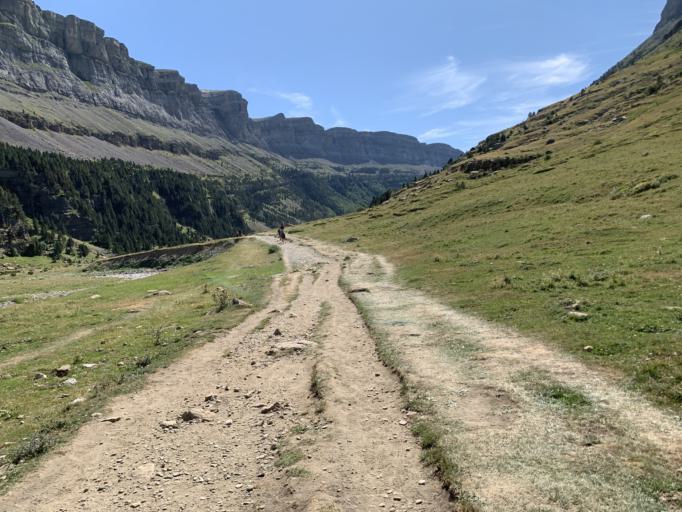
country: ES
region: Aragon
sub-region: Provincia de Huesca
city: Broto
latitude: 42.6443
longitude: 0.0089
